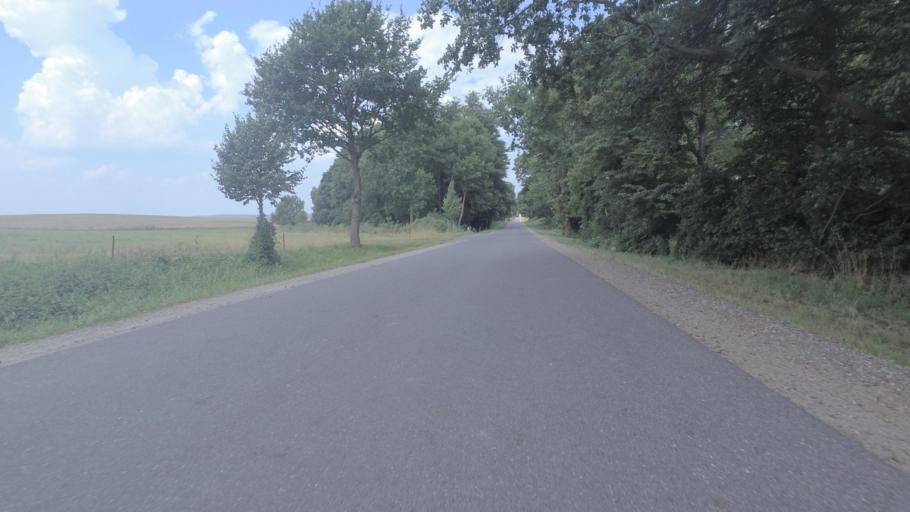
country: DE
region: Mecklenburg-Vorpommern
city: Malchin
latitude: 53.7610
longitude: 12.8360
